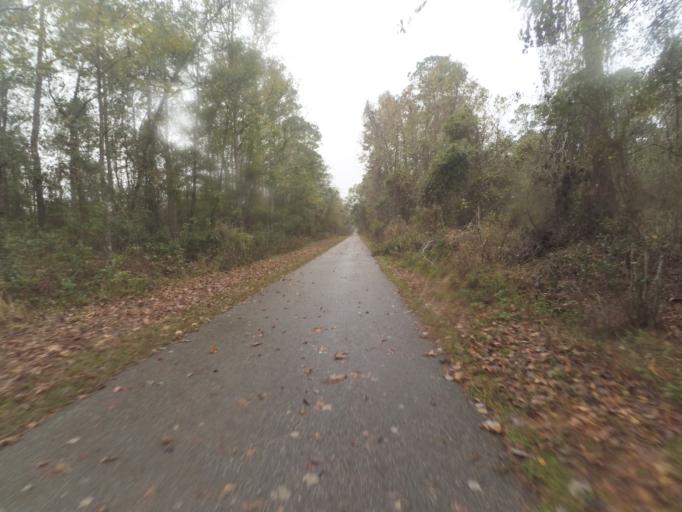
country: US
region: Florida
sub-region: Alachua County
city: Hawthorne
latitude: 29.5874
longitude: -82.0962
